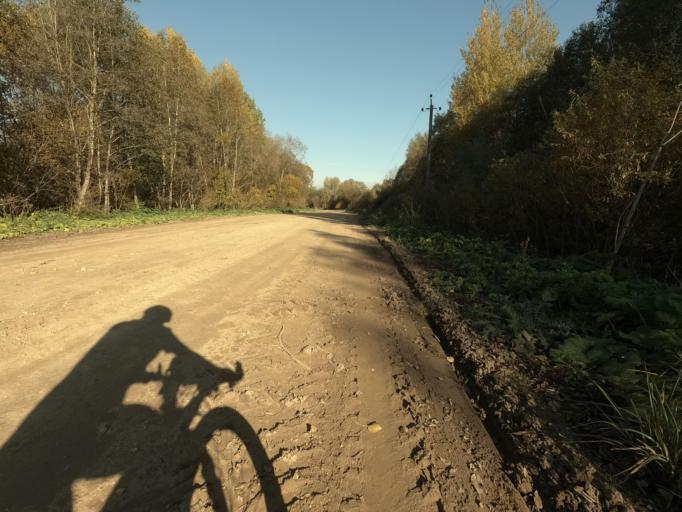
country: RU
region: Novgorod
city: Batetskiy
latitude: 58.8788
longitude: 30.7270
